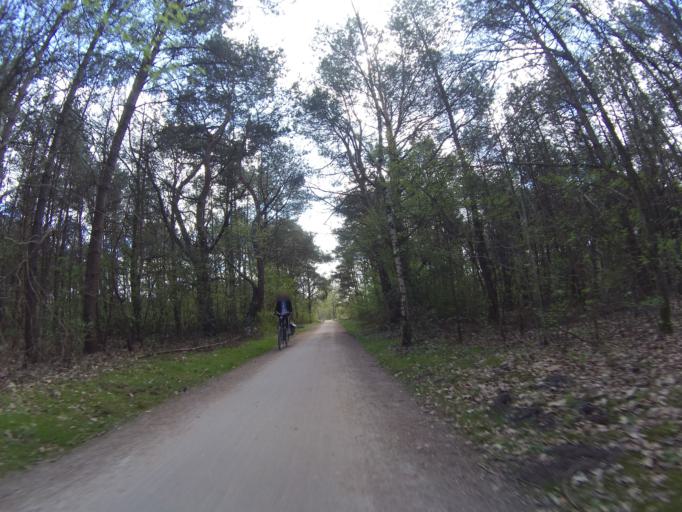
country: NL
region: North Holland
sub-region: Gemeente Bussum
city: Bussum
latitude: 52.2650
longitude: 5.1939
